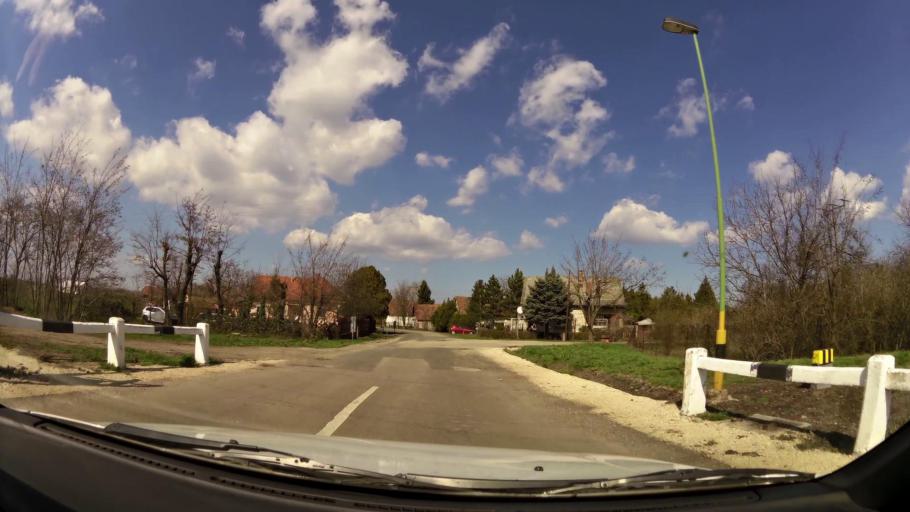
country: HU
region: Pest
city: Tapiogyorgye
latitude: 47.3257
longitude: 19.9467
